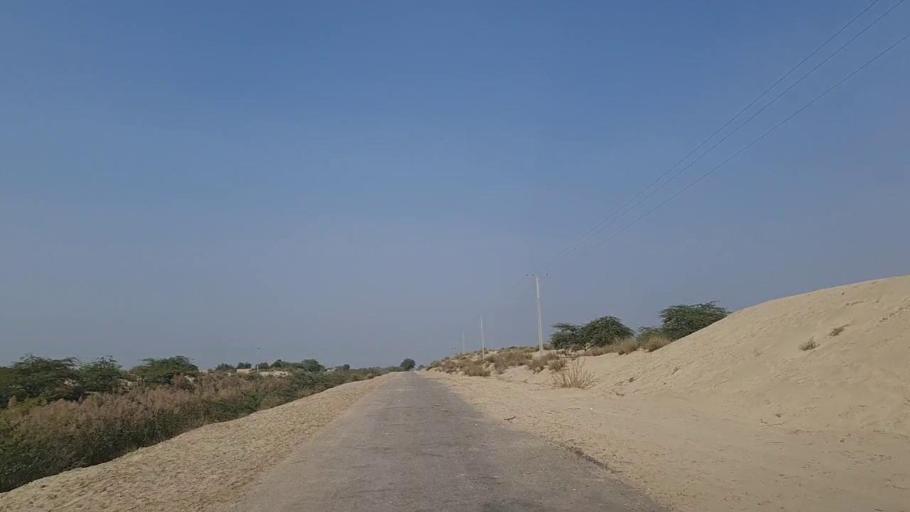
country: PK
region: Sindh
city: Daur
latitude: 26.4618
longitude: 68.4681
